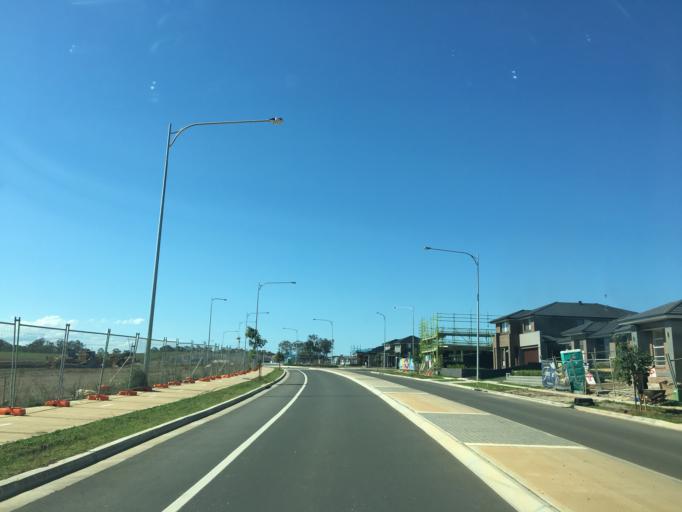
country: AU
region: New South Wales
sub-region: Campbelltown Municipality
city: Denham Court
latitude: -33.9943
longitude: 150.7945
